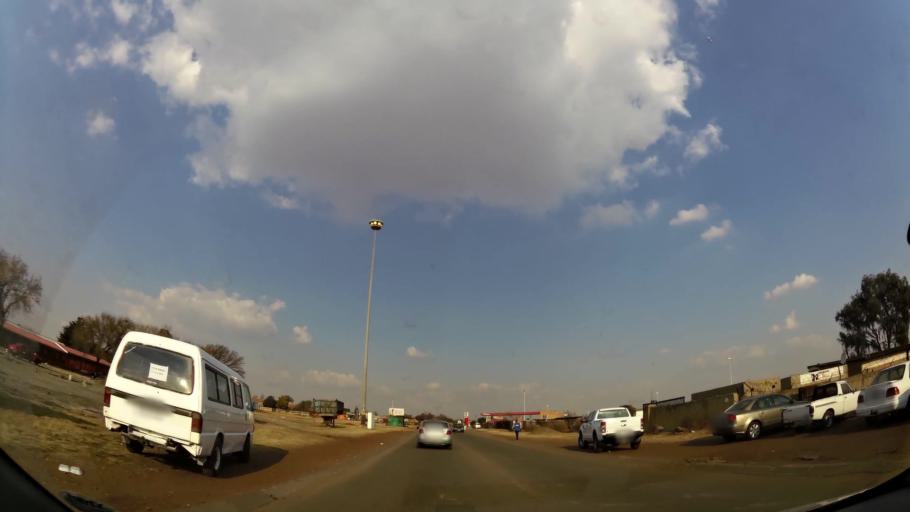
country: ZA
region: Gauteng
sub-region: Ekurhuleni Metropolitan Municipality
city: Germiston
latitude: -26.3480
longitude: 28.1884
